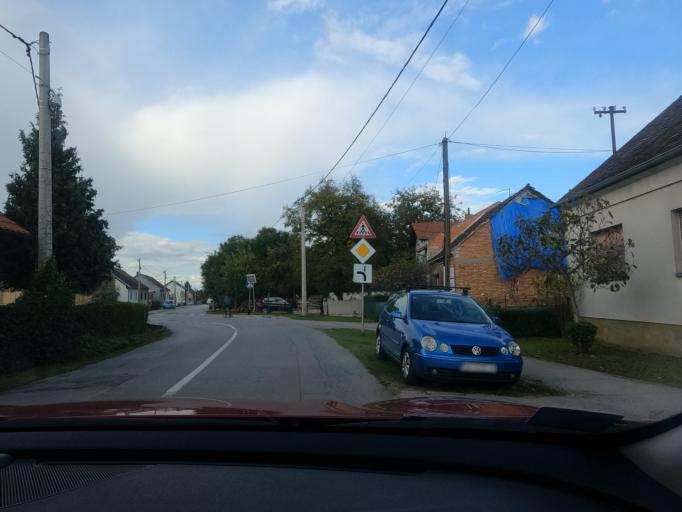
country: HR
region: Sisacko-Moslavacka
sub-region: Grad Sisak
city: Sisak
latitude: 45.4841
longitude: 16.3863
